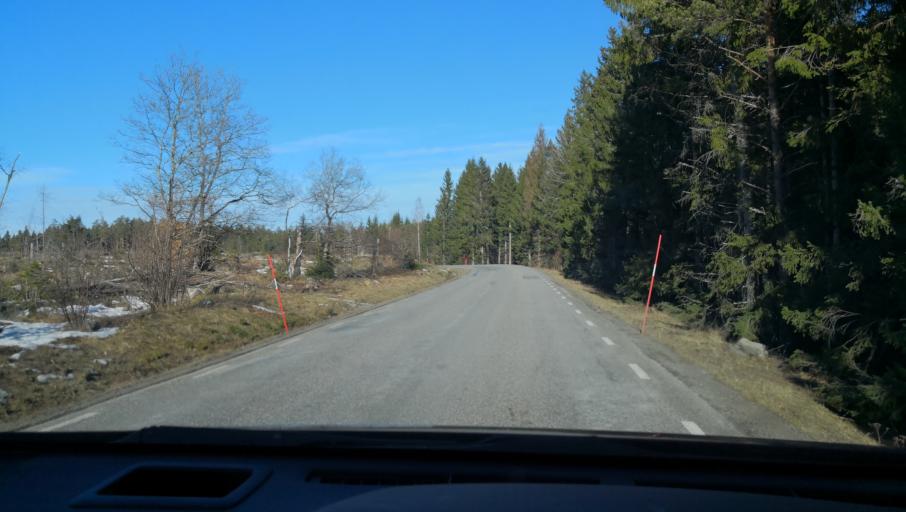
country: SE
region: Uppsala
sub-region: Osthammars Kommun
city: Osterbybruk
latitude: 60.2278
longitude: 17.9193
